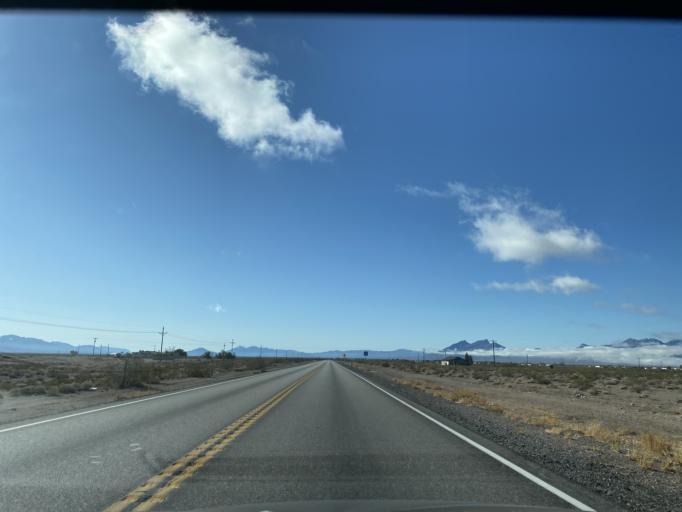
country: US
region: Nevada
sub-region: Nye County
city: Beatty
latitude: 36.5288
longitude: -116.4189
